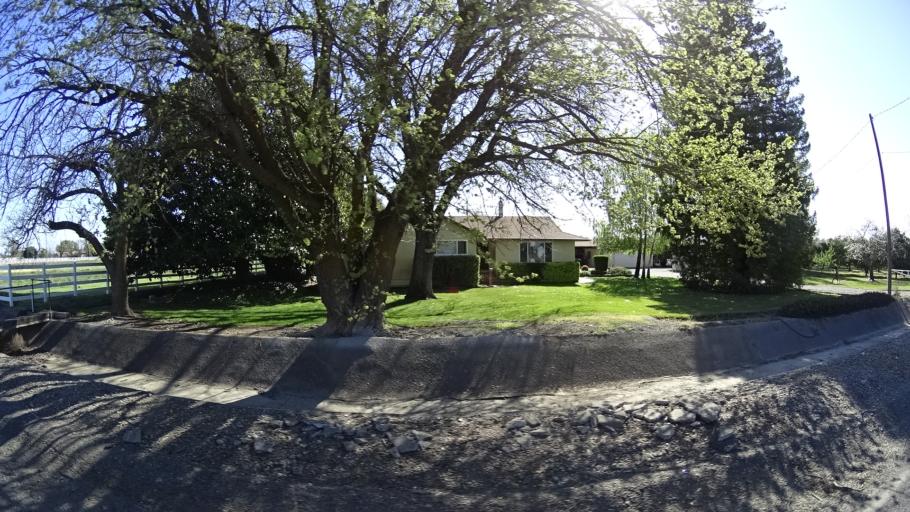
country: US
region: California
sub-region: Glenn County
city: Orland
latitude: 39.7382
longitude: -122.2157
